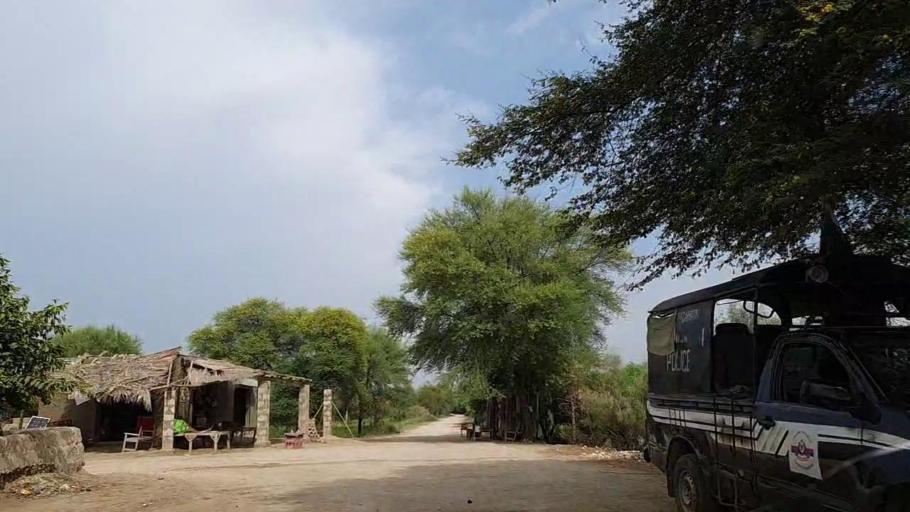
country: PK
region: Sindh
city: Khanpur
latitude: 27.8386
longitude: 69.4846
